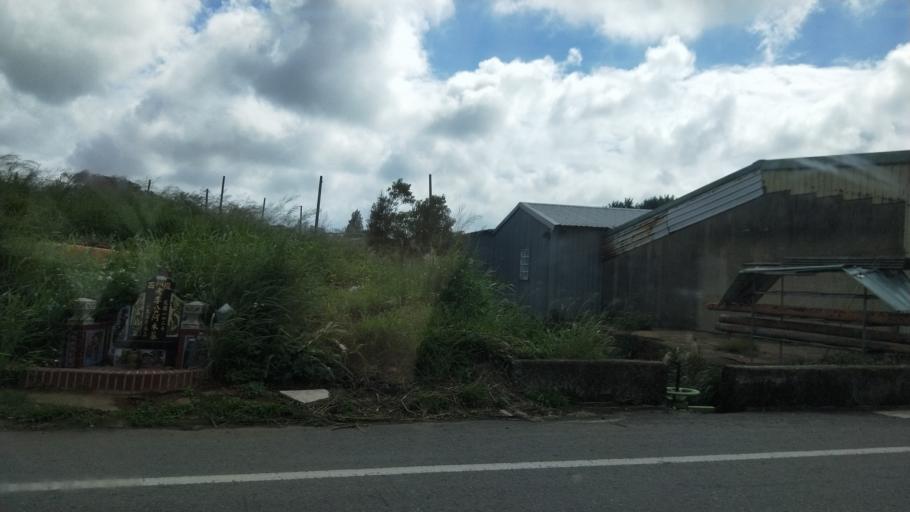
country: TW
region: Taiwan
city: Taoyuan City
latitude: 25.0174
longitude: 121.1369
